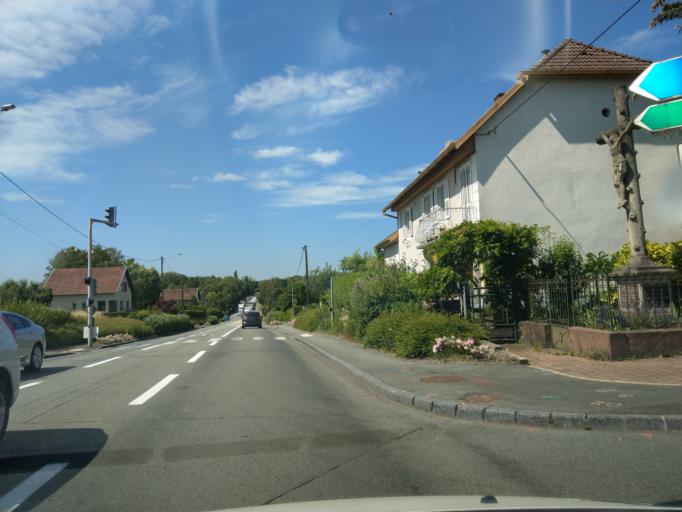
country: FR
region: Franche-Comte
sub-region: Territoire de Belfort
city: Offemont
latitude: 47.6666
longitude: 6.9141
